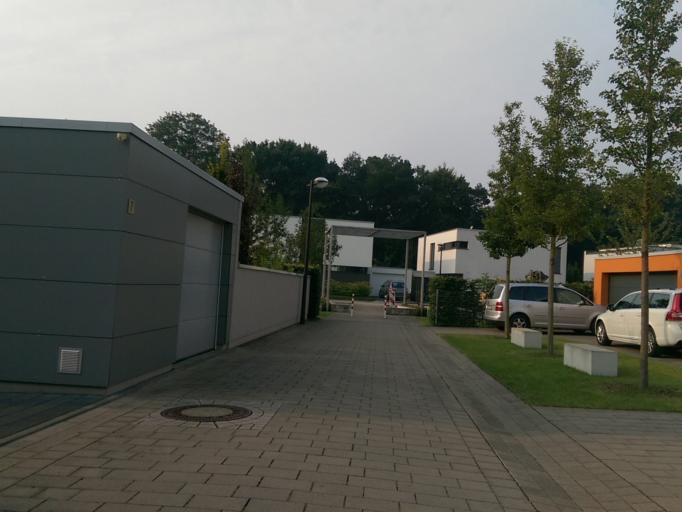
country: DE
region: North Rhine-Westphalia
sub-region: Regierungsbezirk Detmold
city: Guetersloh
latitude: 51.8998
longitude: 8.3511
